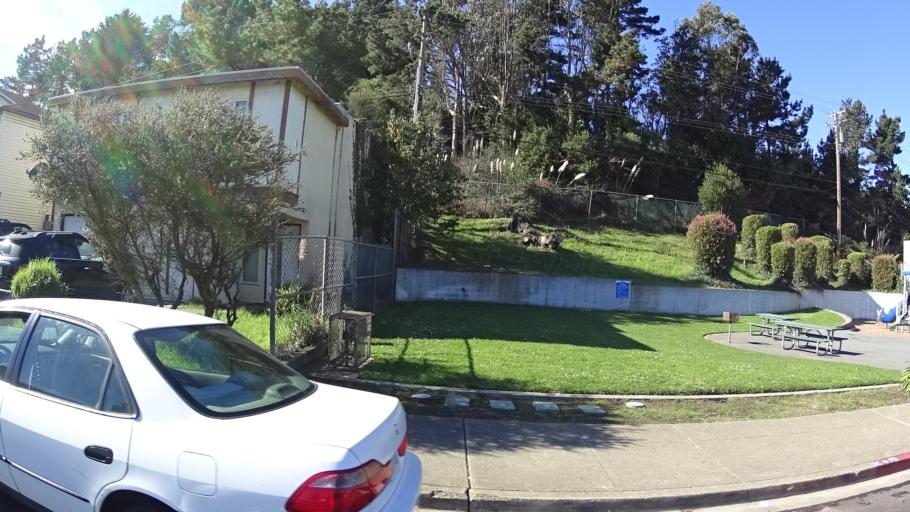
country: US
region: California
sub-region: San Mateo County
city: Colma
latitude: 37.6529
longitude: -122.4703
